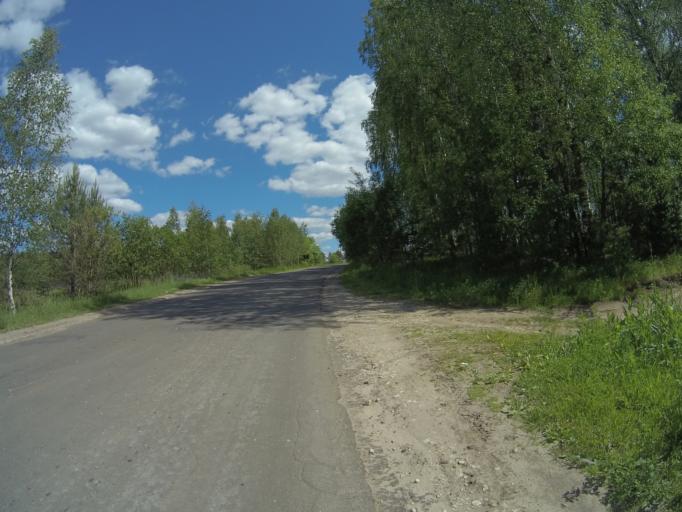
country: RU
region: Vladimir
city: Sudogda
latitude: 56.0740
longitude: 40.7843
